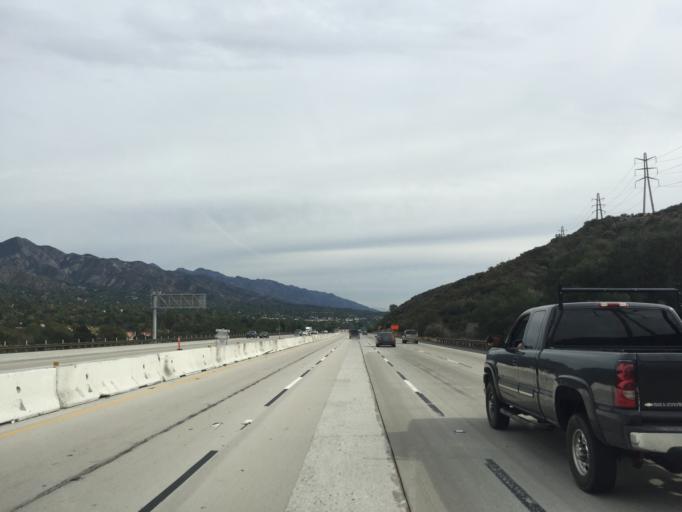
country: US
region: California
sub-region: Los Angeles County
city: La Crescenta-Montrose
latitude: 34.2335
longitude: -118.2769
